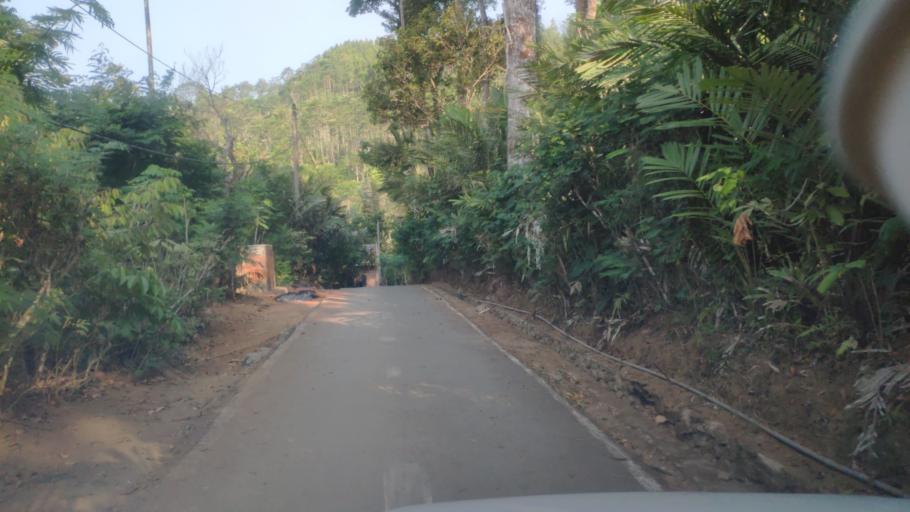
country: ID
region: Central Java
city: Wonosobo
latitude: -7.4245
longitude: 109.7399
